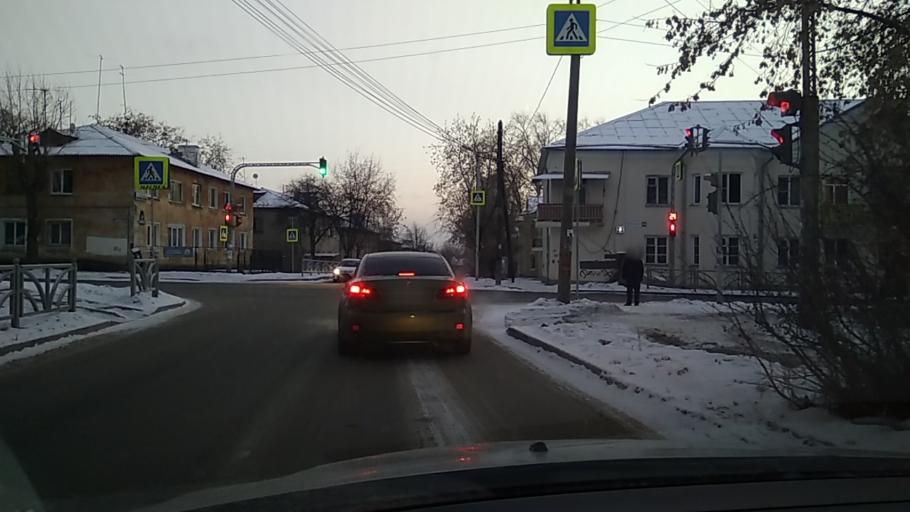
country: RU
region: Sverdlovsk
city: Istok
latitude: 56.7627
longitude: 60.7114
